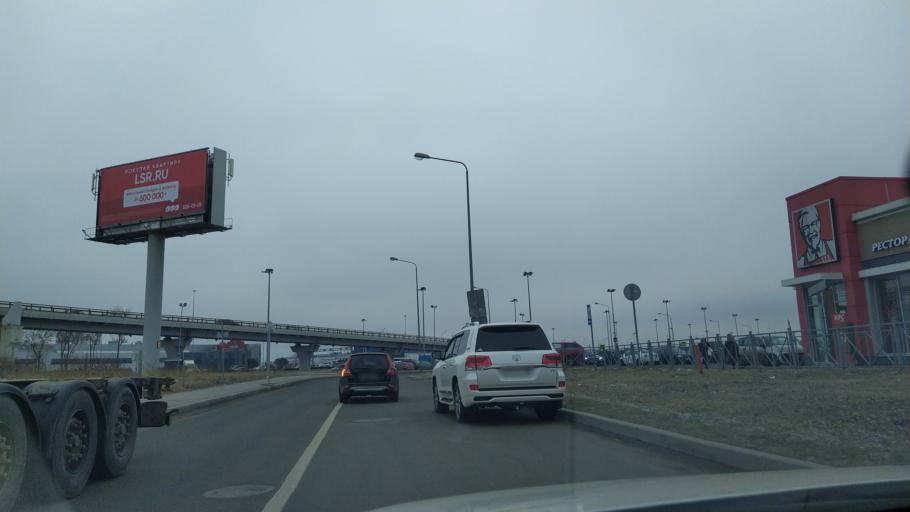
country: RU
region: St.-Petersburg
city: Kupchino
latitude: 59.8094
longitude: 30.3209
